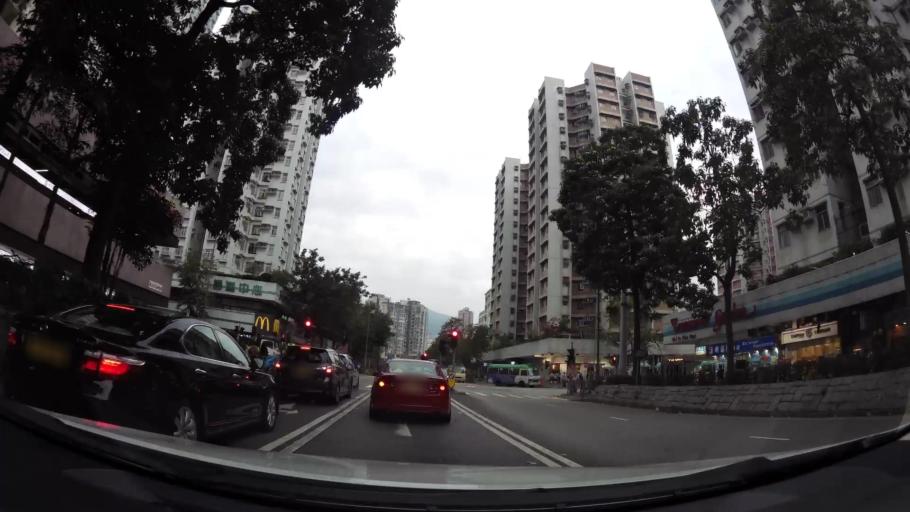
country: HK
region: Tai Po
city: Tai Po
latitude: 22.4532
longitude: 114.1674
